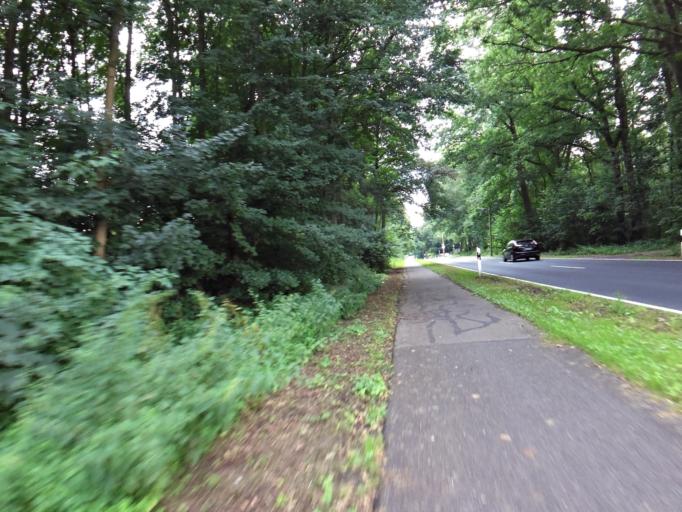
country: DE
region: North Rhine-Westphalia
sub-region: Regierungsbezirk Koln
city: Selfkant
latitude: 51.0033
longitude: 5.9324
